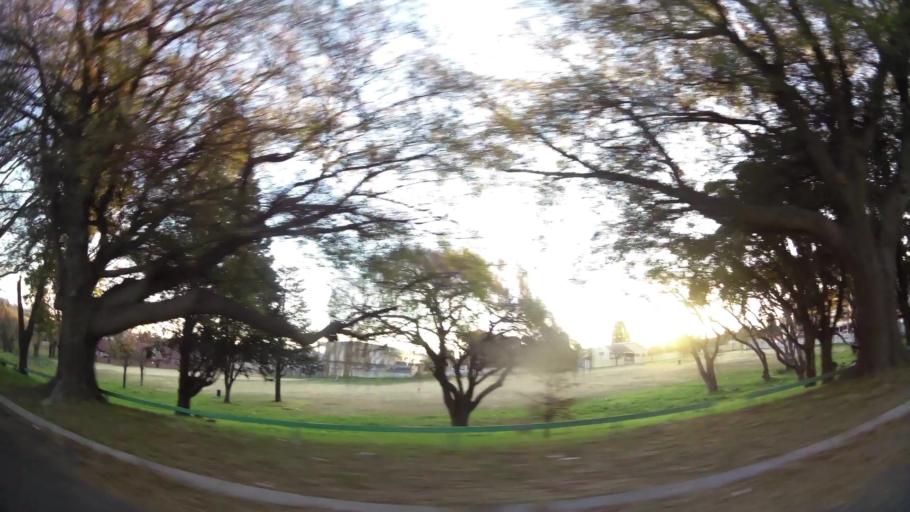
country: ZA
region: Gauteng
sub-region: City of Johannesburg Metropolitan Municipality
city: Roodepoort
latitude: -26.1562
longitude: 27.8877
